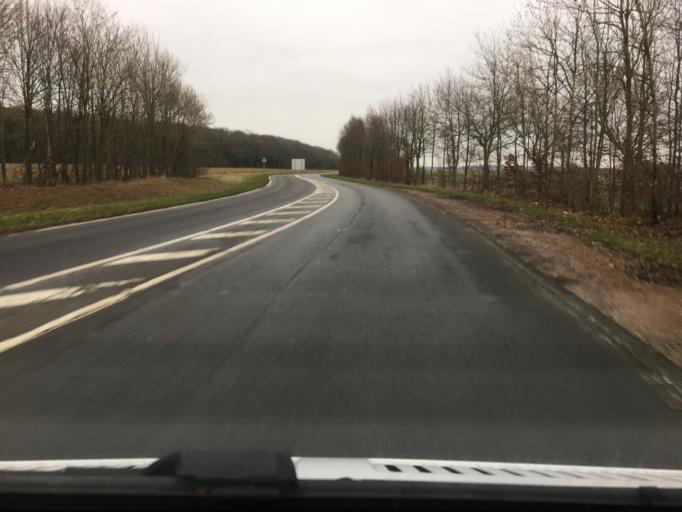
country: FR
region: Picardie
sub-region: Departement de la Somme
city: Pende
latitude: 50.1820
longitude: 1.5965
